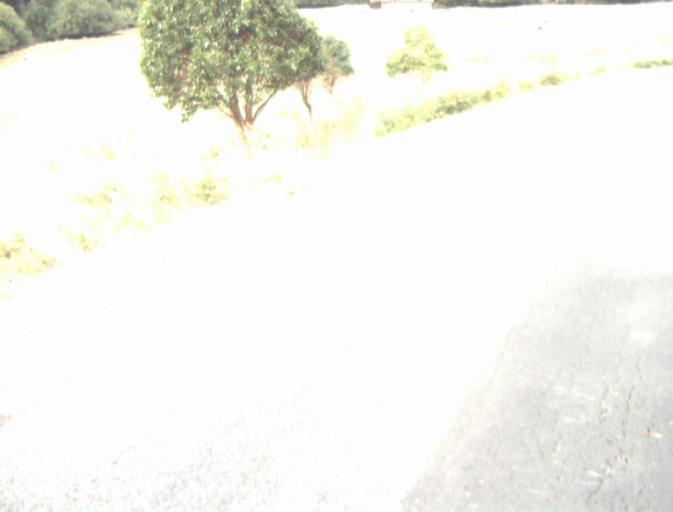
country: AU
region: Tasmania
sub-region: Dorset
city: Scottsdale
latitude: -41.4646
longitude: 147.5936
